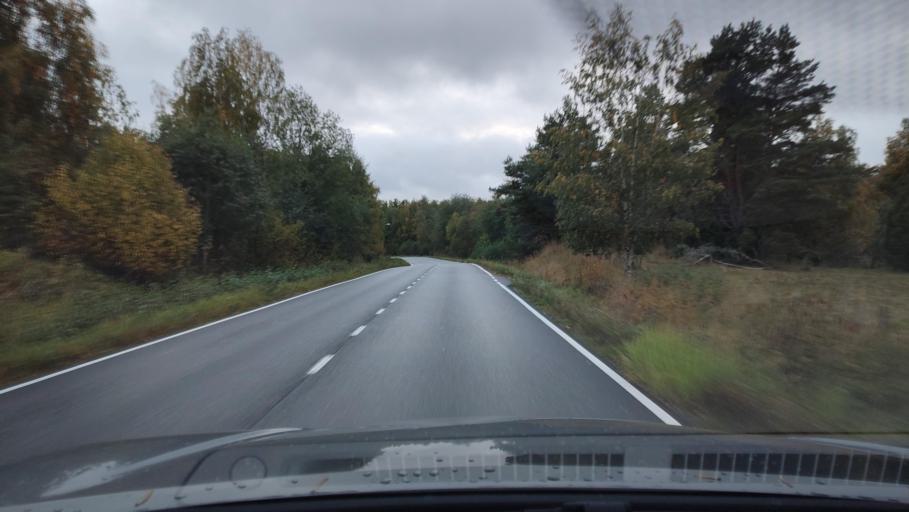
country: FI
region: Ostrobothnia
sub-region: Sydosterbotten
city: Kristinestad
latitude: 62.2788
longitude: 21.4006
